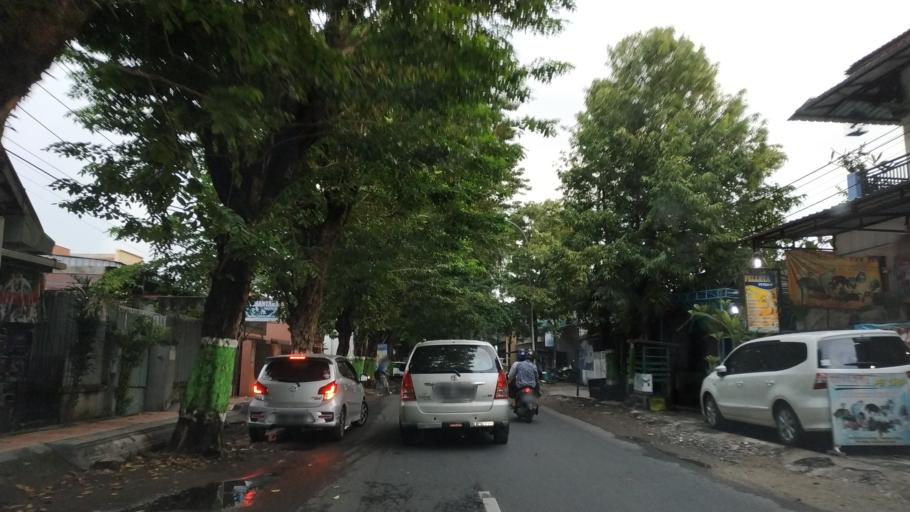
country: ID
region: Central Java
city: Kudus
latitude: -6.8080
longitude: 110.8555
